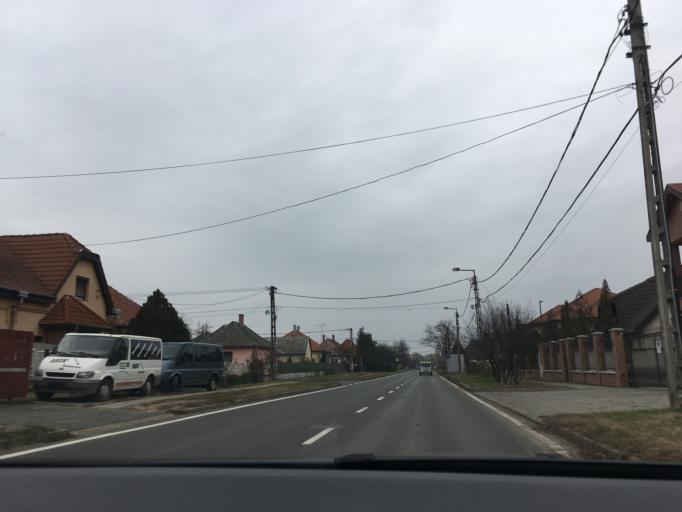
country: HU
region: Hajdu-Bihar
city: Debrecen
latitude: 47.5322
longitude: 21.6712
